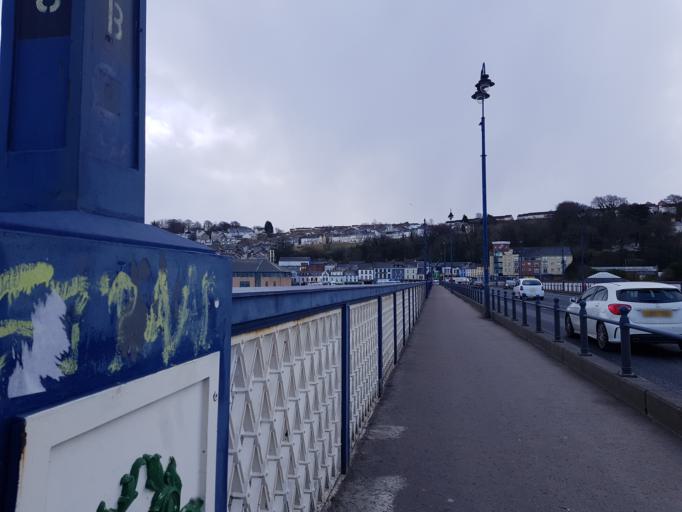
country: GB
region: Northern Ireland
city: Londonderry County Borough
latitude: 54.9910
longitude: -7.3186
